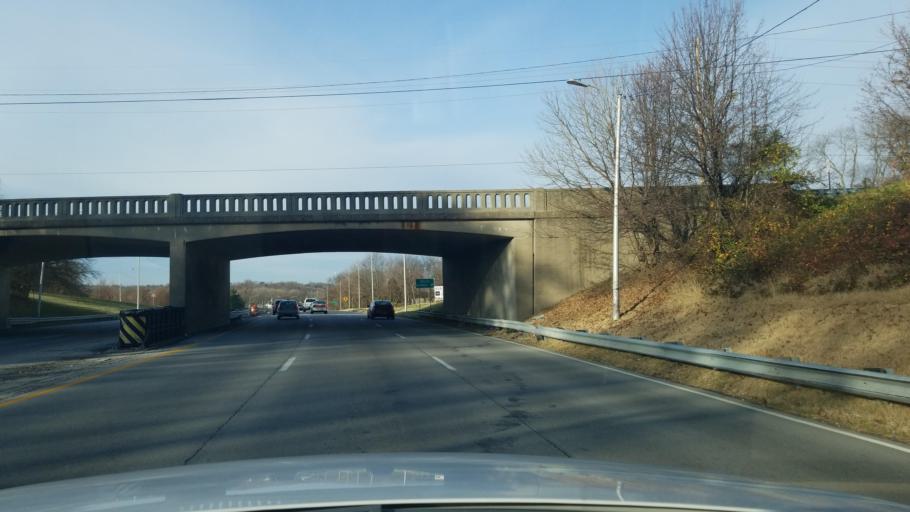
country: US
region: Indiana
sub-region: Vanderburgh County
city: Evansville
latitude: 37.9783
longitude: -87.6093
